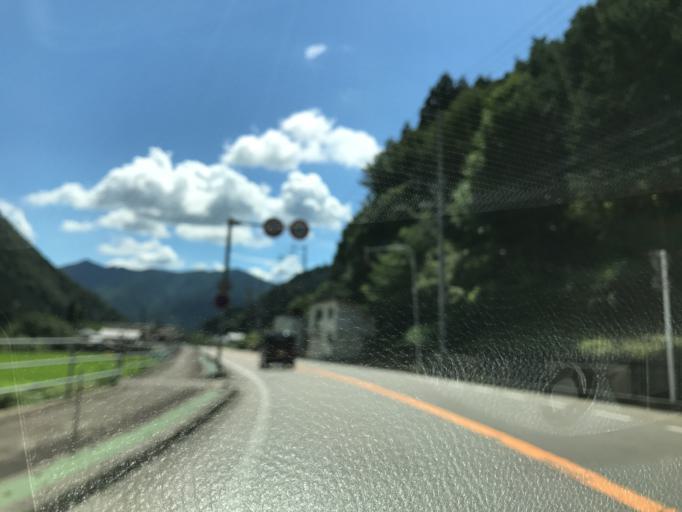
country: JP
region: Gifu
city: Gujo
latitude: 35.8579
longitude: 137.0406
